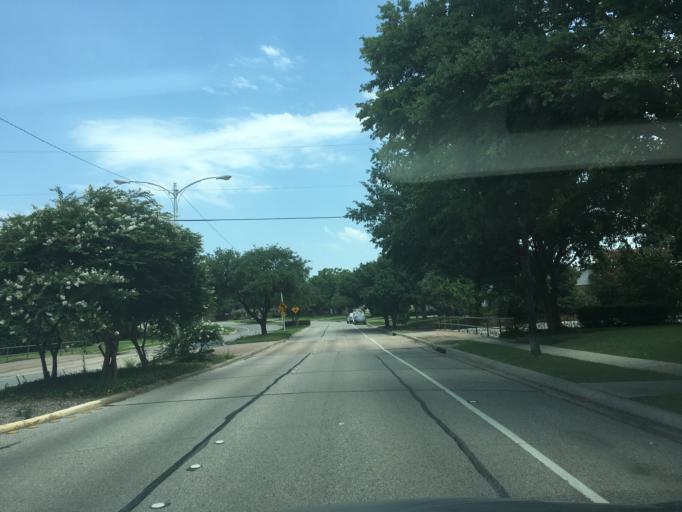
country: US
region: Texas
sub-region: Dallas County
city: Carrollton
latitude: 32.9374
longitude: -96.8698
